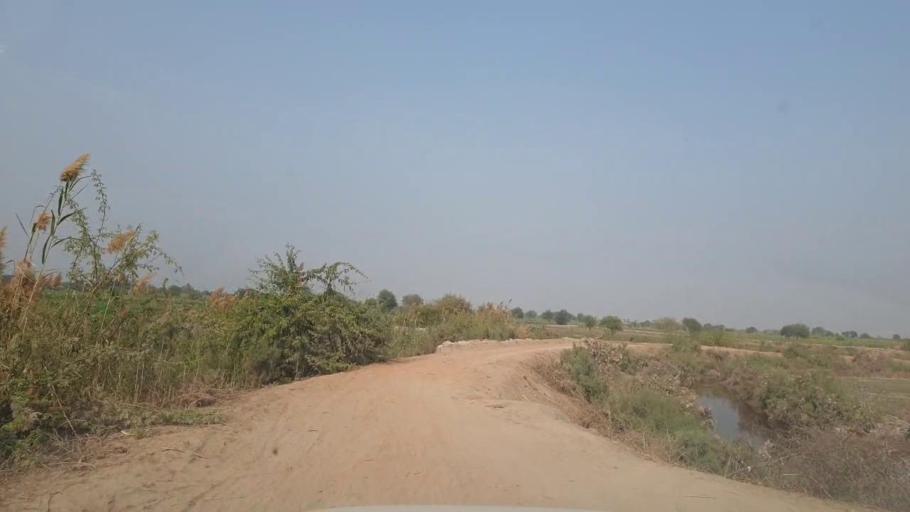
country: PK
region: Sindh
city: Mirpur Khas
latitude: 25.5751
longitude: 69.1357
